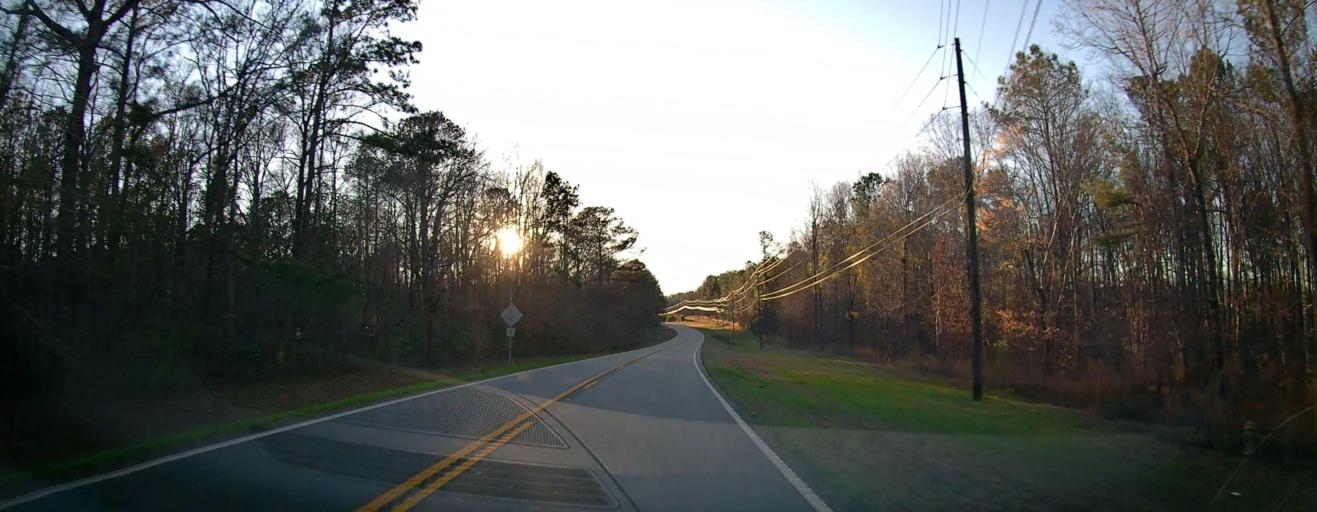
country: US
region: Georgia
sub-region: Harris County
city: Hamilton
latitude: 32.6726
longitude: -84.9227
